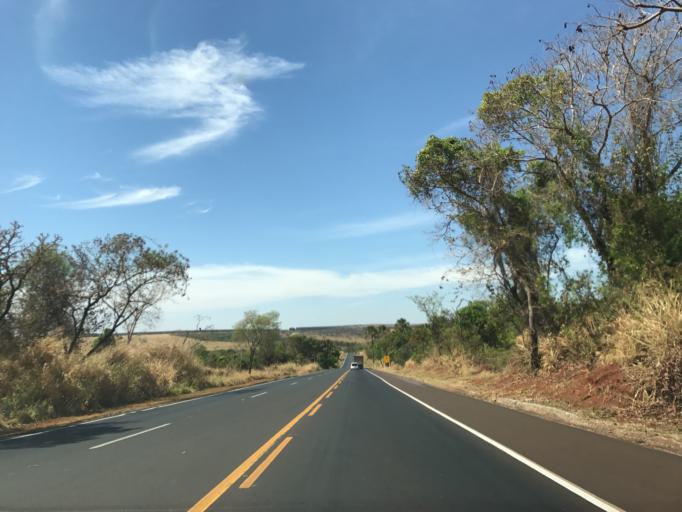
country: BR
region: Minas Gerais
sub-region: Monte Alegre De Minas
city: Monte Alegre de Minas
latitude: -19.0775
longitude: -48.9995
